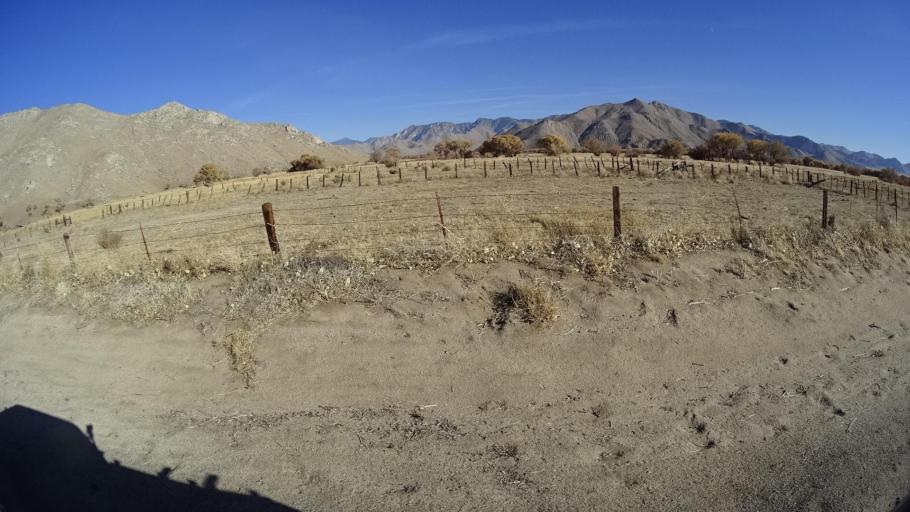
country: US
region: California
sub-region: Kern County
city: Weldon
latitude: 35.6843
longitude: -118.2902
